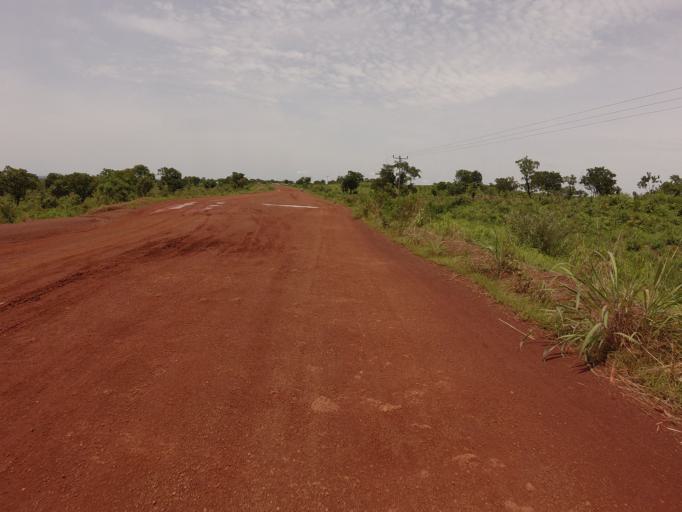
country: GH
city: Kpandae
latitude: 8.7414
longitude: 0.0800
